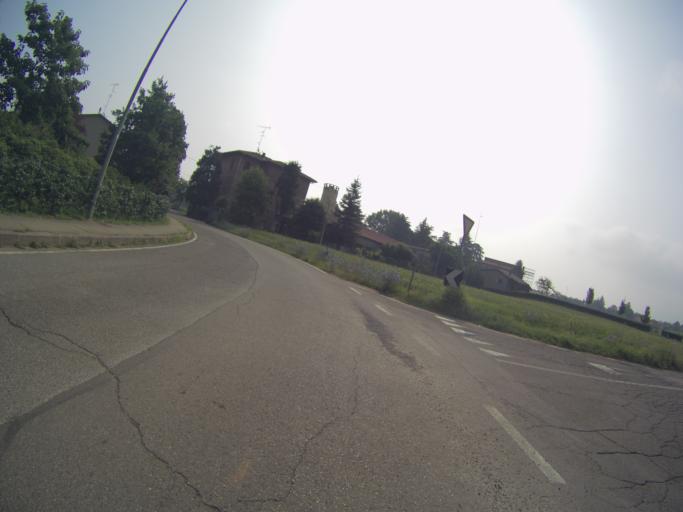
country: IT
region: Emilia-Romagna
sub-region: Provincia di Reggio Emilia
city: Borzano
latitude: 44.5987
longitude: 10.6394
